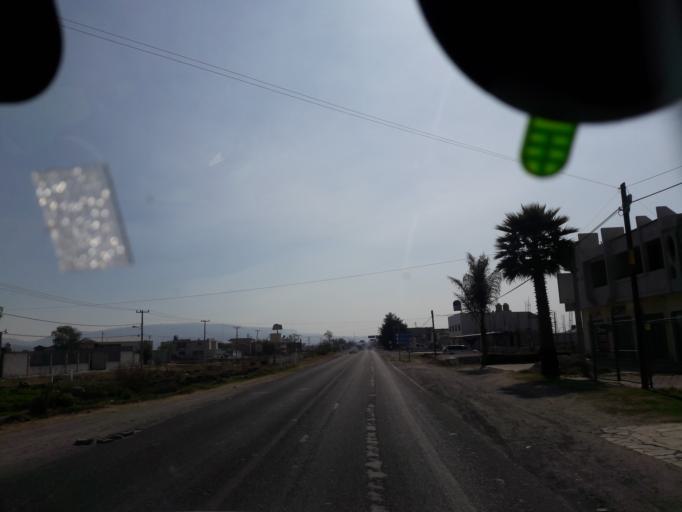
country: MX
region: Tlaxcala
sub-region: Ixtacuixtla de Mariano Matamoros
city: Santa Justina Ecatepec
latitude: 19.3108
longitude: -98.3484
